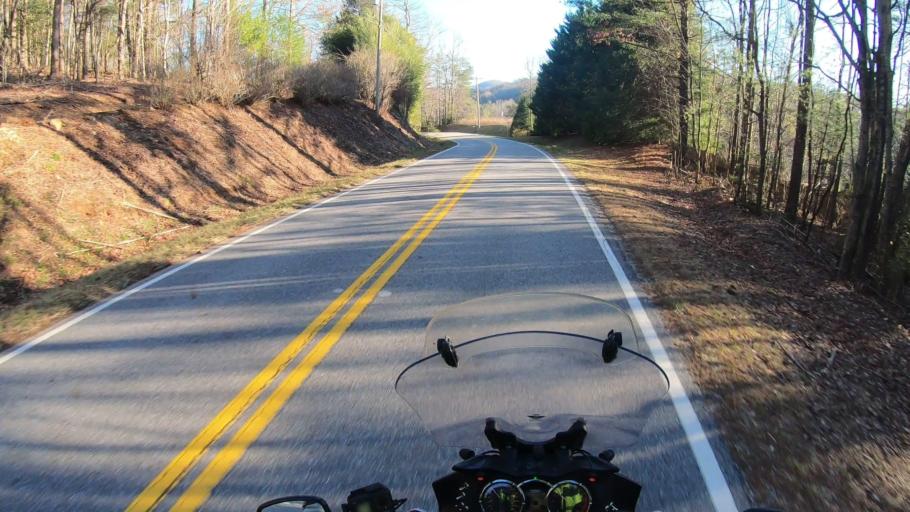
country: US
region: Georgia
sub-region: Lumpkin County
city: Dahlonega
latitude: 34.7078
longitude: -84.0420
